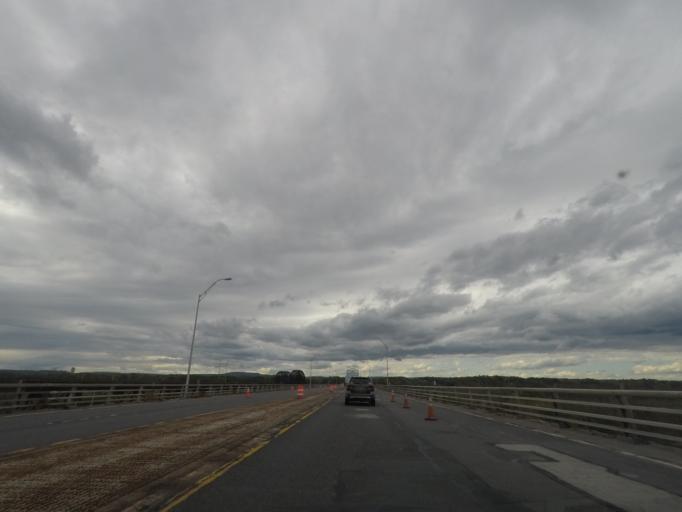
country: US
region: New York
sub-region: Rensselaer County
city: Castleton-on-Hudson
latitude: 42.5070
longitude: -73.7651
